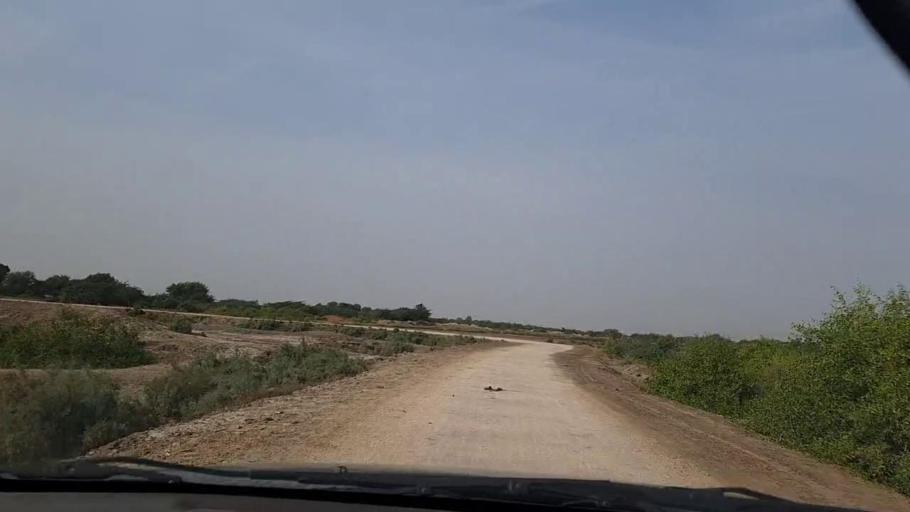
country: PK
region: Sindh
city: Thatta
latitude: 24.6096
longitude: 67.9541
